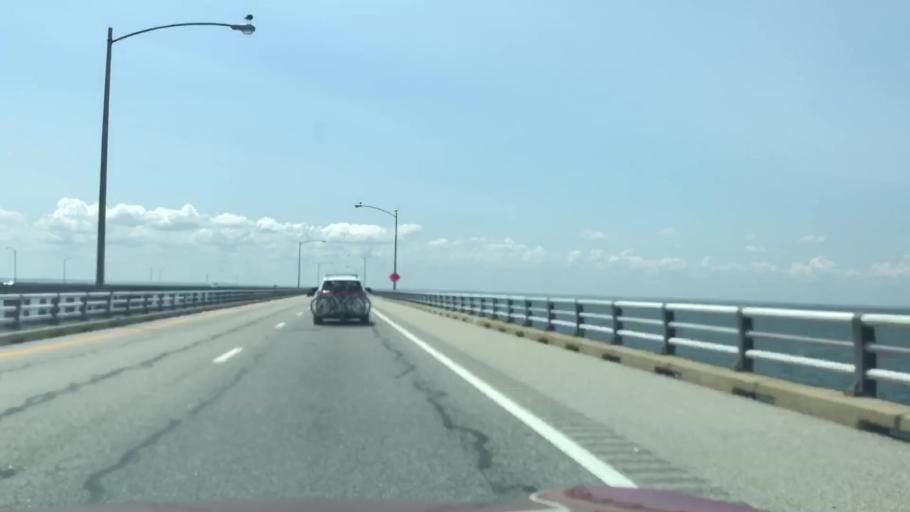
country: US
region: Virginia
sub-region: City of Virginia Beach
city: Virginia Beach
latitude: 37.0062
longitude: -76.0968
